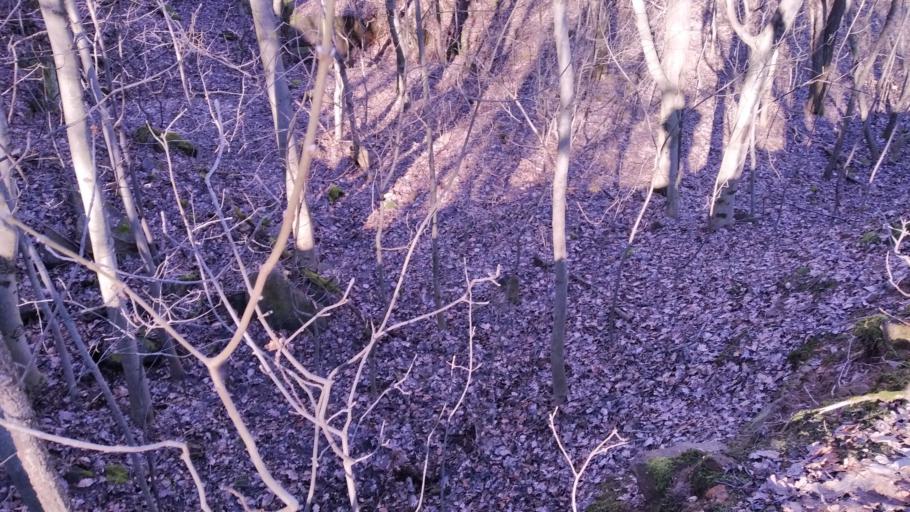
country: HU
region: Pest
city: Urom
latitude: 47.6123
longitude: 19.0103
